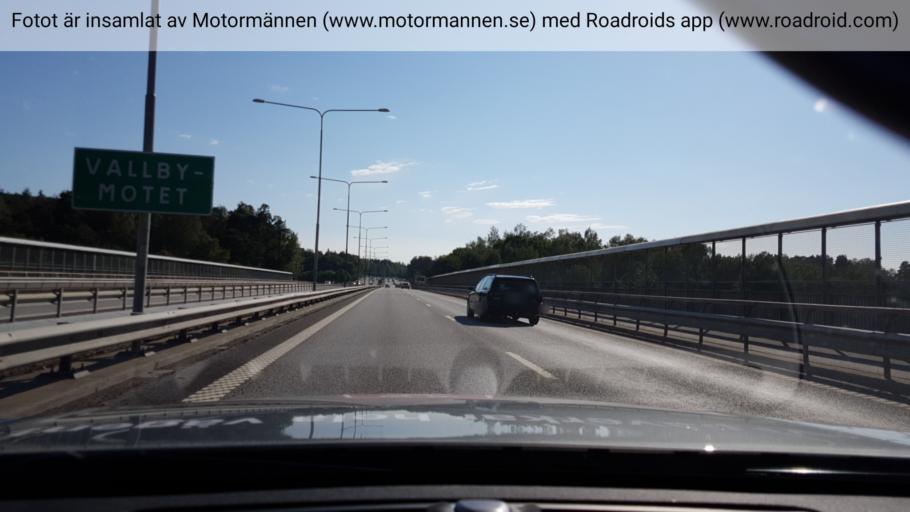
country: SE
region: Vaestmanland
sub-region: Vasteras
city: Vasteras
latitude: 59.6223
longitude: 16.5232
